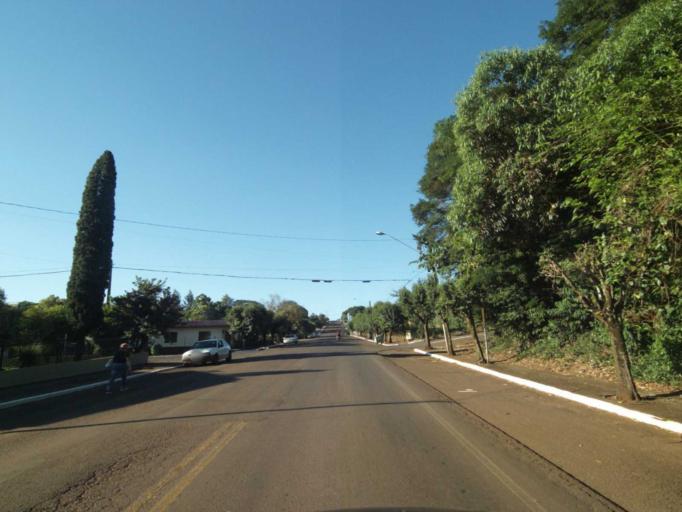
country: BR
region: Parana
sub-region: Coronel Vivida
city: Coronel Vivida
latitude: -25.9626
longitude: -52.8139
